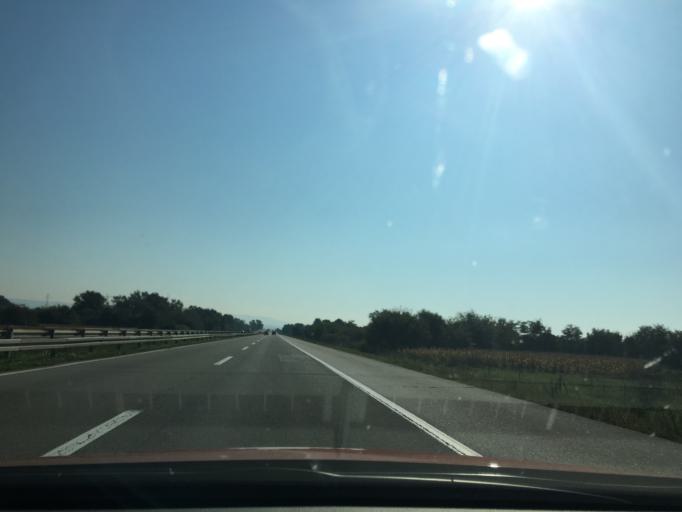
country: RS
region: Central Serbia
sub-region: Pomoravski Okrug
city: Cuprija
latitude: 43.9619
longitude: 21.3331
